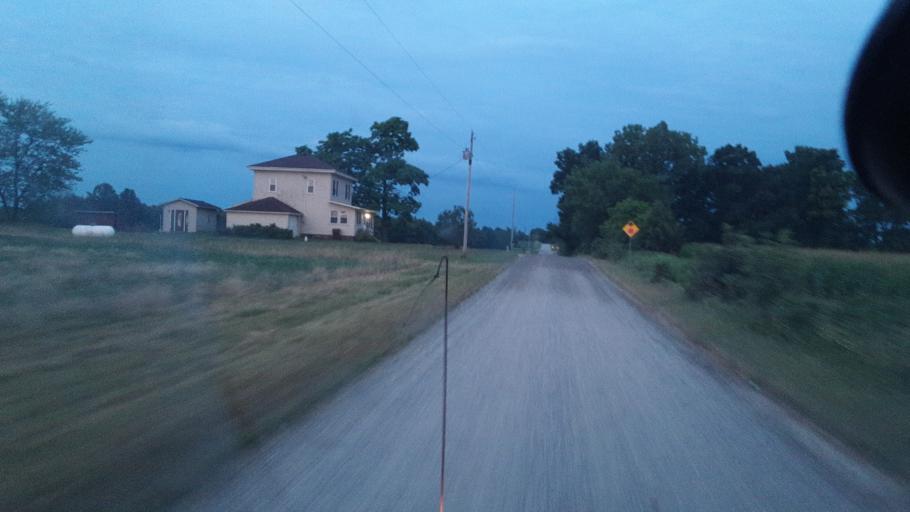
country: US
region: Ohio
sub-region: Defiance County
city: Hicksville
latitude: 41.3444
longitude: -84.8305
